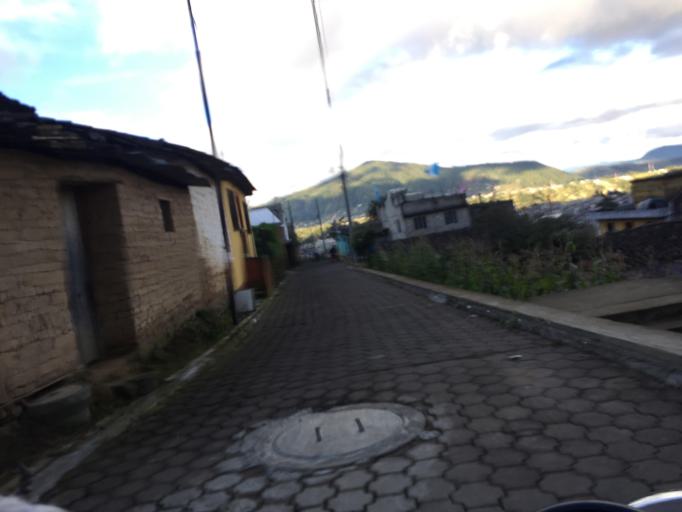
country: GT
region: Totonicapan
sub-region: Municipio de Totonicapan
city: Totonicapan
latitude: 14.9148
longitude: -91.3538
